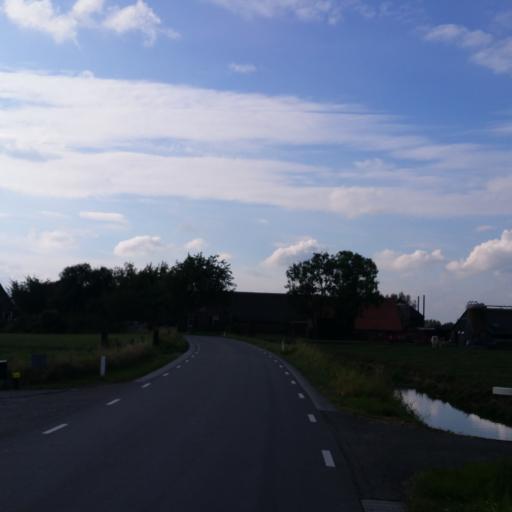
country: NL
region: Utrecht
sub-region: Gemeente IJsselstein
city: IJsselstein
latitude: 52.0376
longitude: 5.0208
